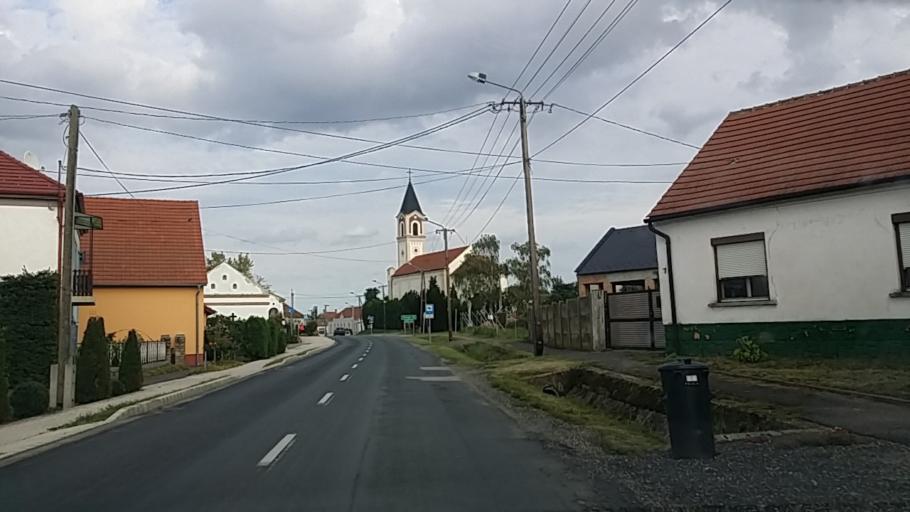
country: HU
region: Gyor-Moson-Sopron
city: Nagycenk
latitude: 47.6208
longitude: 16.7632
